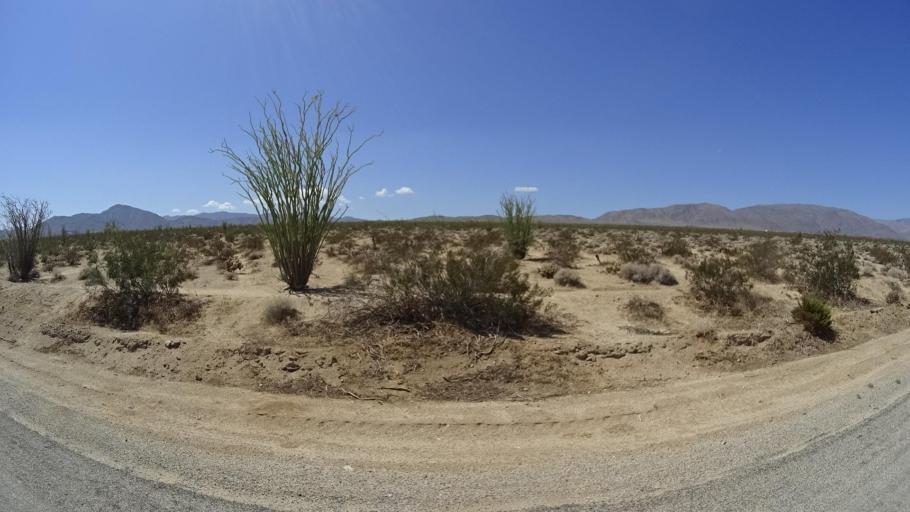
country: US
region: California
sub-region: San Diego County
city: Borrego Springs
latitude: 33.1848
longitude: -116.2876
